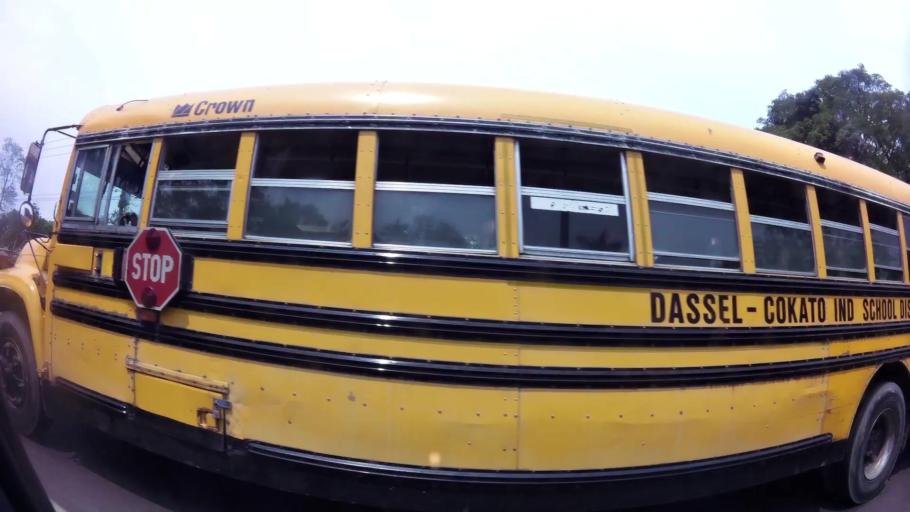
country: HN
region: Cortes
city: Nuevo Chamelecon
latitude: 15.3785
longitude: -87.9887
